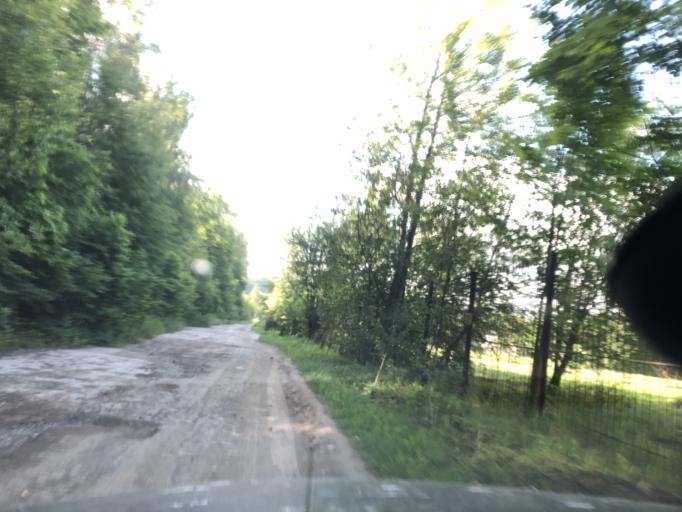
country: RU
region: Tula
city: Shvartsevskiy
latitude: 54.2541
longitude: 37.9251
